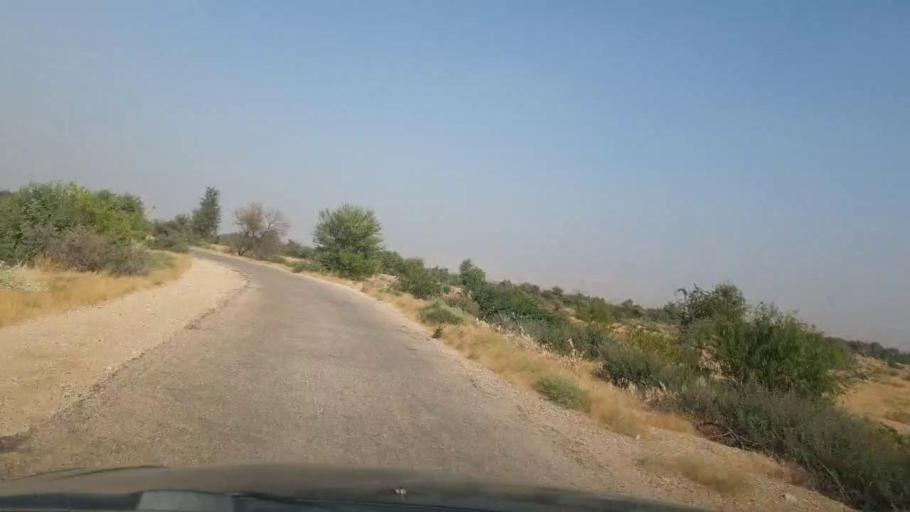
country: PK
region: Sindh
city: Jamshoro
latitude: 25.5296
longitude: 67.8226
